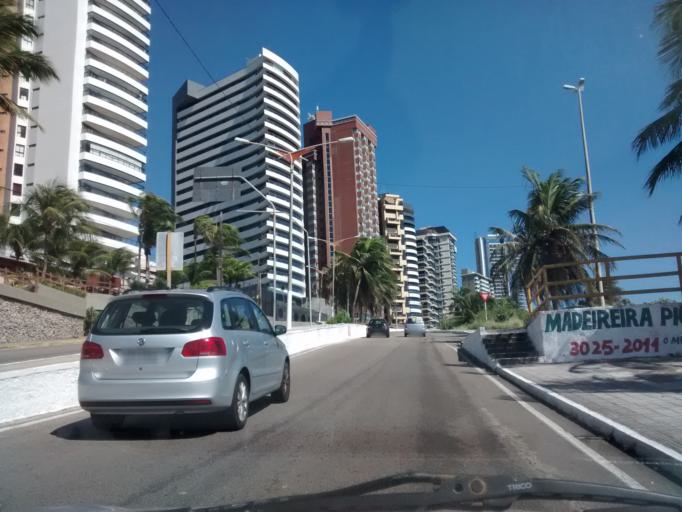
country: BR
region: Rio Grande do Norte
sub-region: Natal
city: Natal
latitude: -5.7840
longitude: -35.1922
